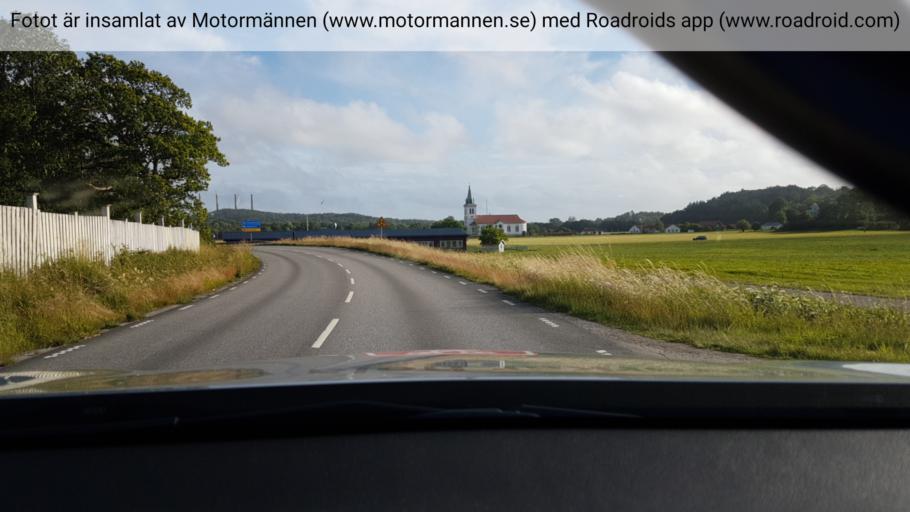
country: SE
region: Vaestra Goetaland
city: Svanesund
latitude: 58.1084
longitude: 11.8516
